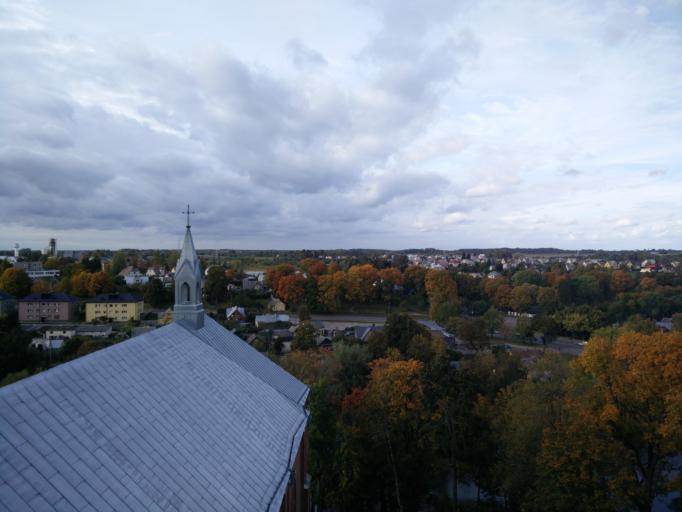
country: LT
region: Utenos apskritis
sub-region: Anyksciai
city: Anyksciai
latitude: 55.5243
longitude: 25.1007
